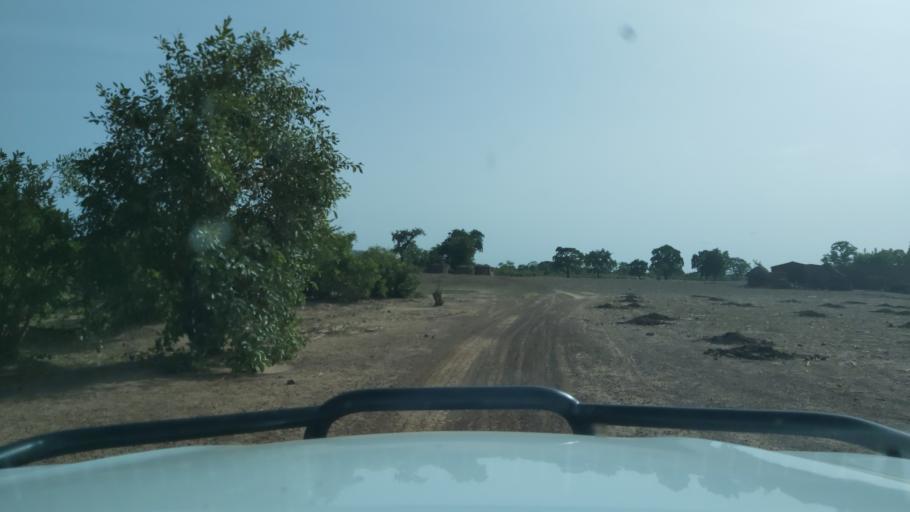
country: ML
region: Koulikoro
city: Koulikoro
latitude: 13.1759
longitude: -7.7550
